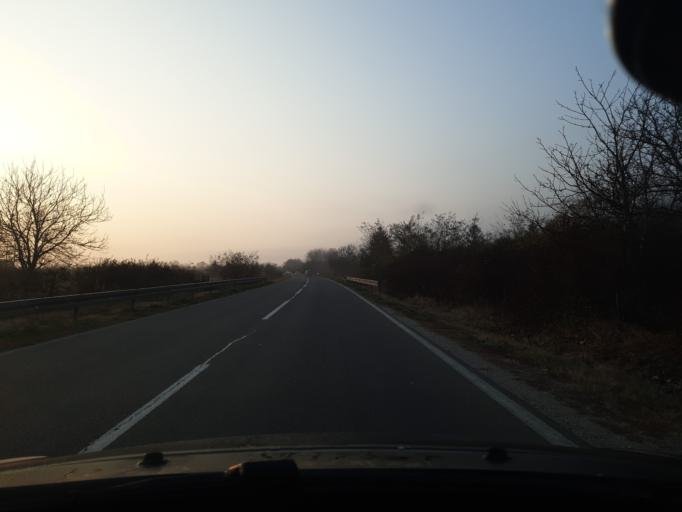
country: RS
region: Central Serbia
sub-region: Jablanicki Okrug
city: Leskovac
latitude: 42.9694
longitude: 21.9767
